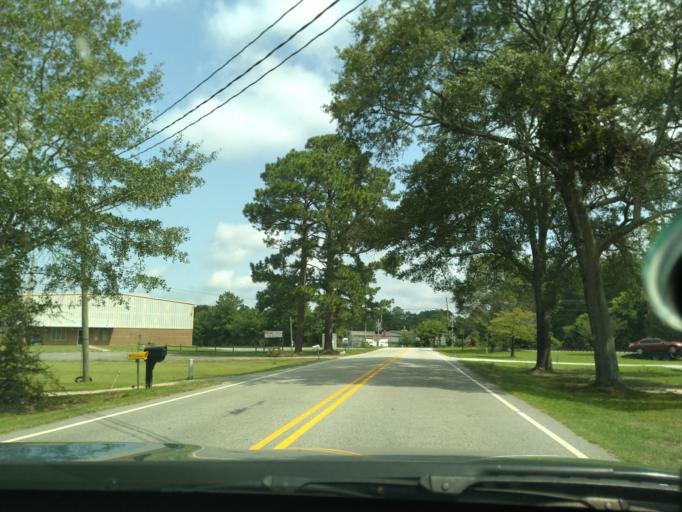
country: US
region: North Carolina
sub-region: Edgecombe County
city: Princeville
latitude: 35.8764
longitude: -77.5222
